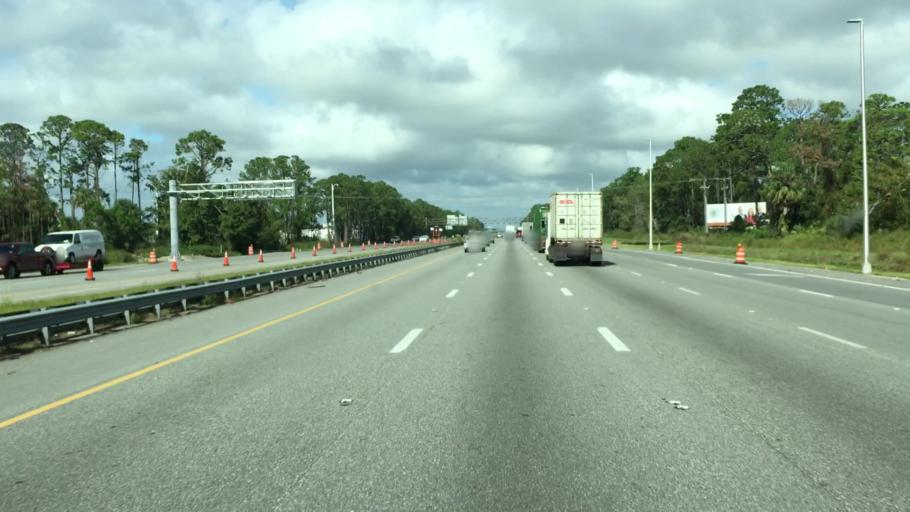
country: US
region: Florida
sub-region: Volusia County
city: Daytona Beach
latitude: 29.1835
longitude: -81.0904
